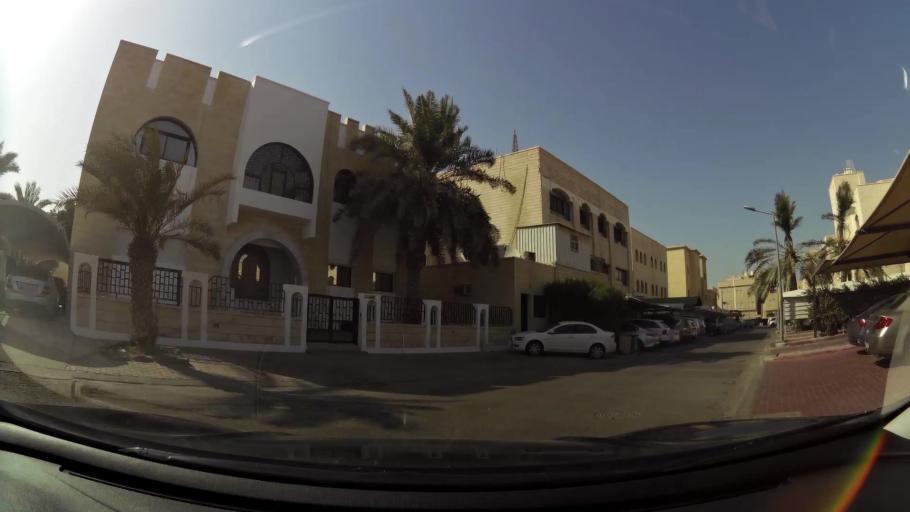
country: KW
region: Muhafazat Hawalli
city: Salwa
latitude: 29.2877
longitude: 48.0792
